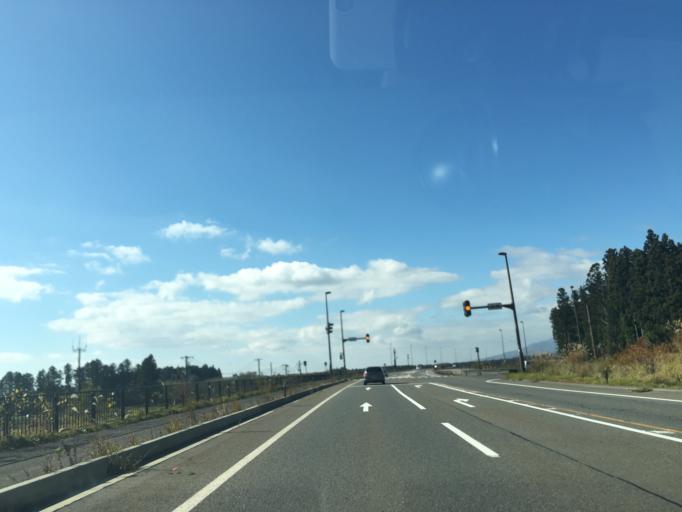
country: JP
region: Fukushima
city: Inawashiro
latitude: 37.5142
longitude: 140.1321
